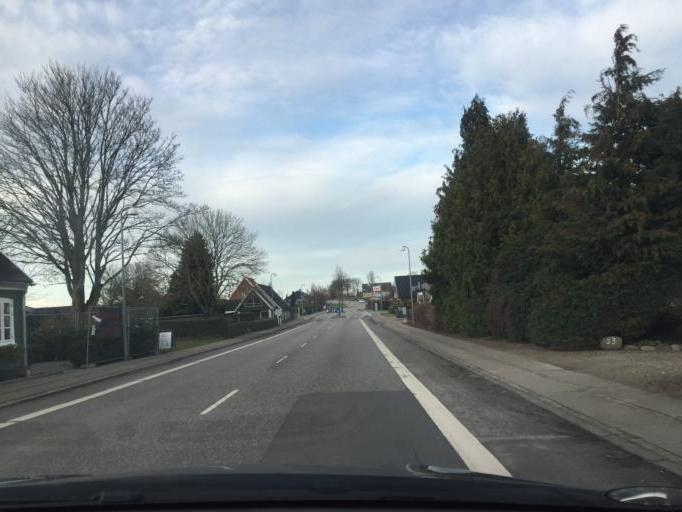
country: DK
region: South Denmark
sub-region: Faaborg-Midtfyn Kommune
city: Ringe
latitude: 55.2449
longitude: 10.4765
